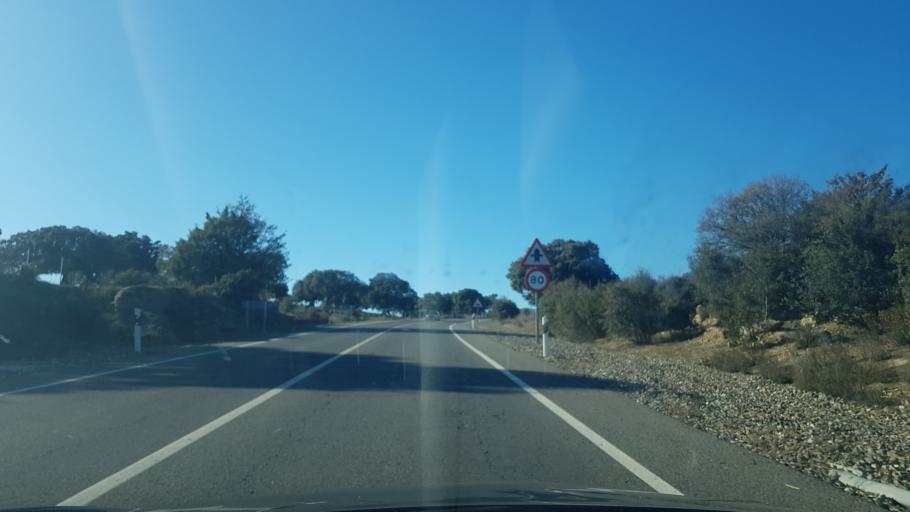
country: ES
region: Castille and Leon
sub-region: Provincia de Avila
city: Barraco
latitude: 40.4628
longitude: -4.6182
